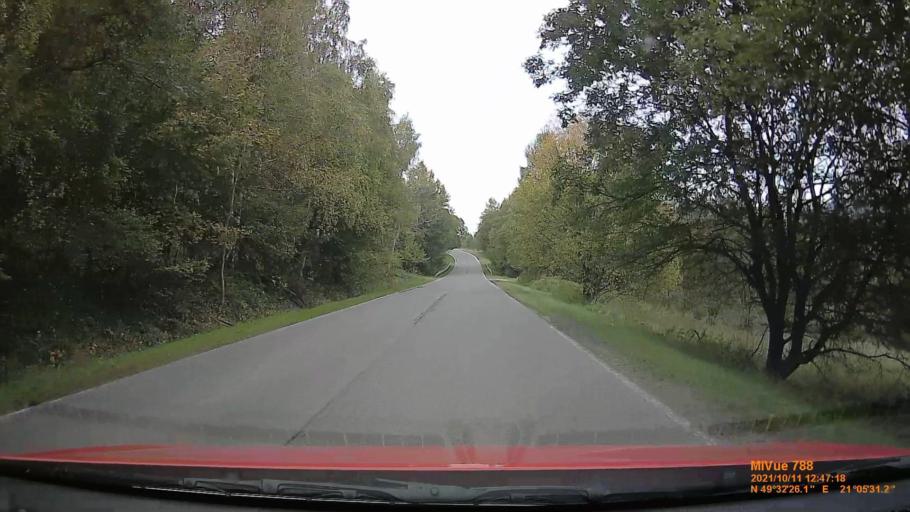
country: PL
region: Lesser Poland Voivodeship
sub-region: Powiat gorlicki
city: Uscie Gorlickie
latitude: 49.5407
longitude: 21.0918
